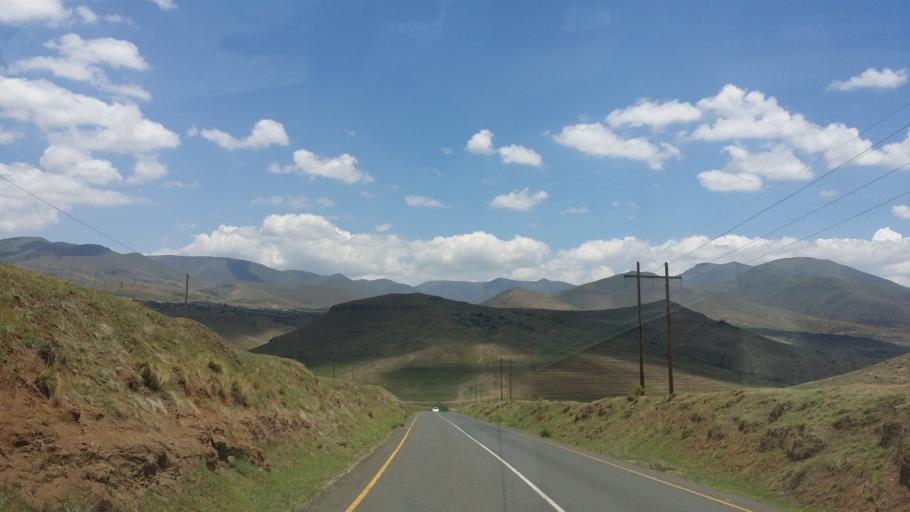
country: LS
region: Mokhotlong
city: Mokhotlong
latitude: -29.2140
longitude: 28.8930
